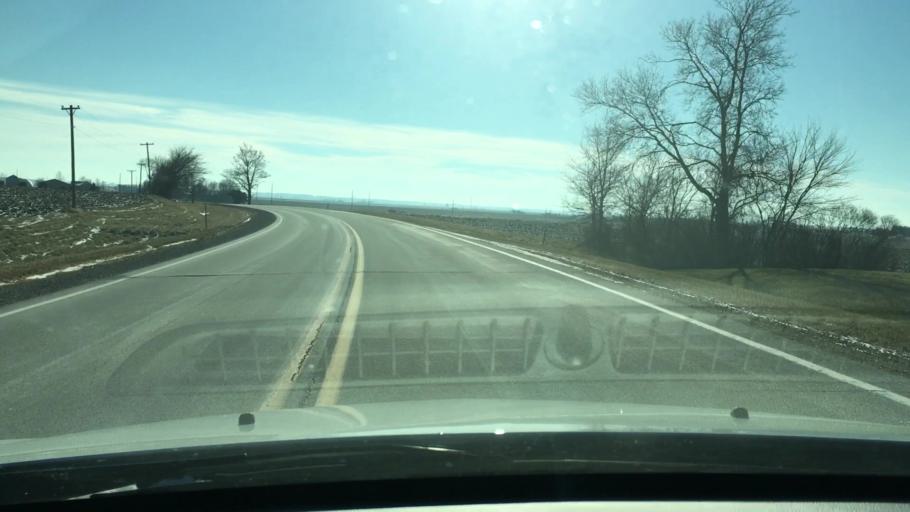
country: US
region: Illinois
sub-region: Ogle County
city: Rochelle
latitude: 41.8376
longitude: -89.0829
